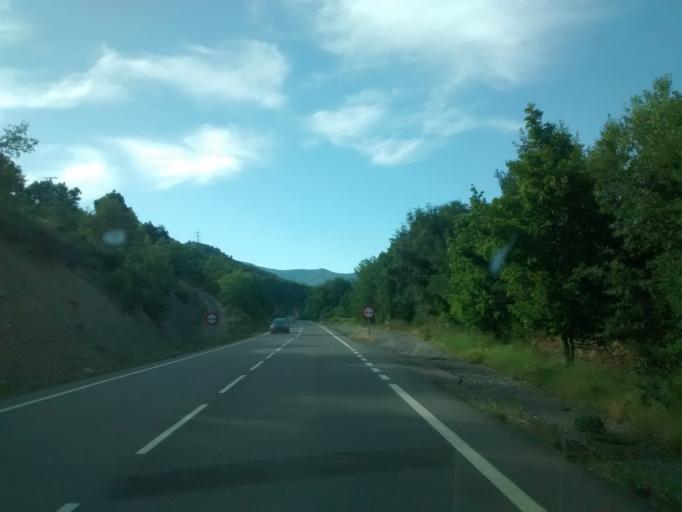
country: ES
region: Aragon
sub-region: Provincia de Huesca
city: Ainsa
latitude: 42.4303
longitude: 0.1341
